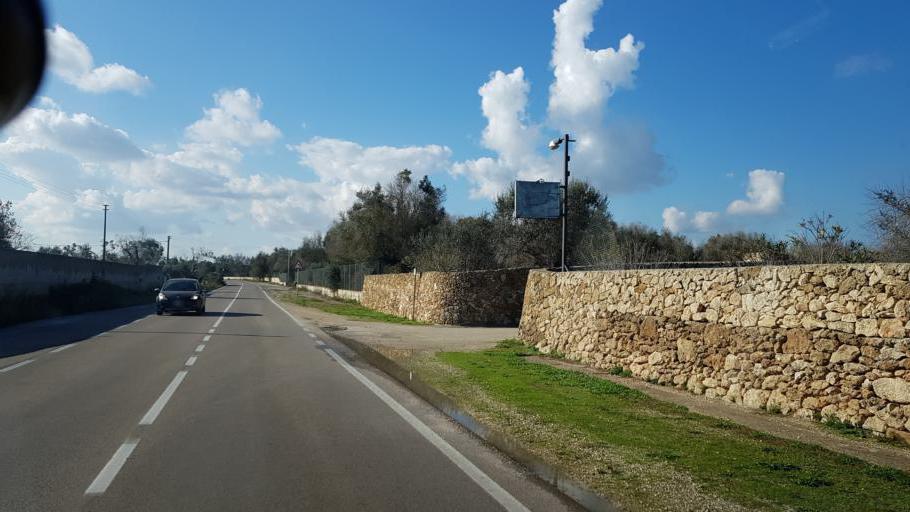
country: IT
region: Apulia
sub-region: Provincia di Lecce
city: Trepuzzi
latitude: 40.4425
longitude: 18.0926
